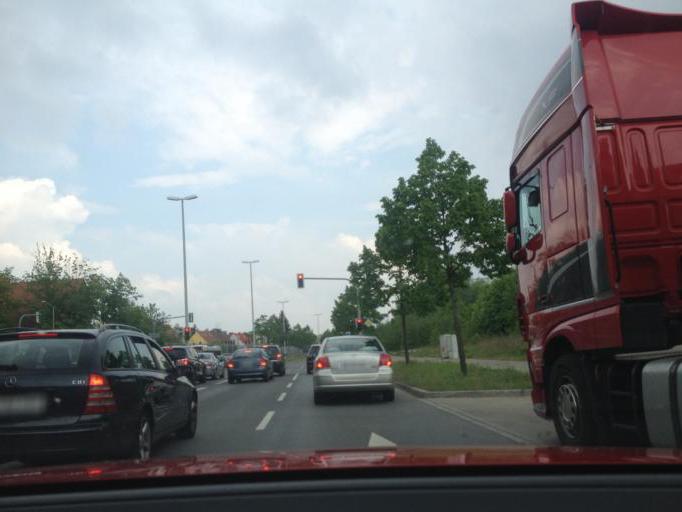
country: DE
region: Bavaria
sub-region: Regierungsbezirk Mittelfranken
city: Grossreuth bei Schweinau
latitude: 49.4412
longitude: 11.0228
